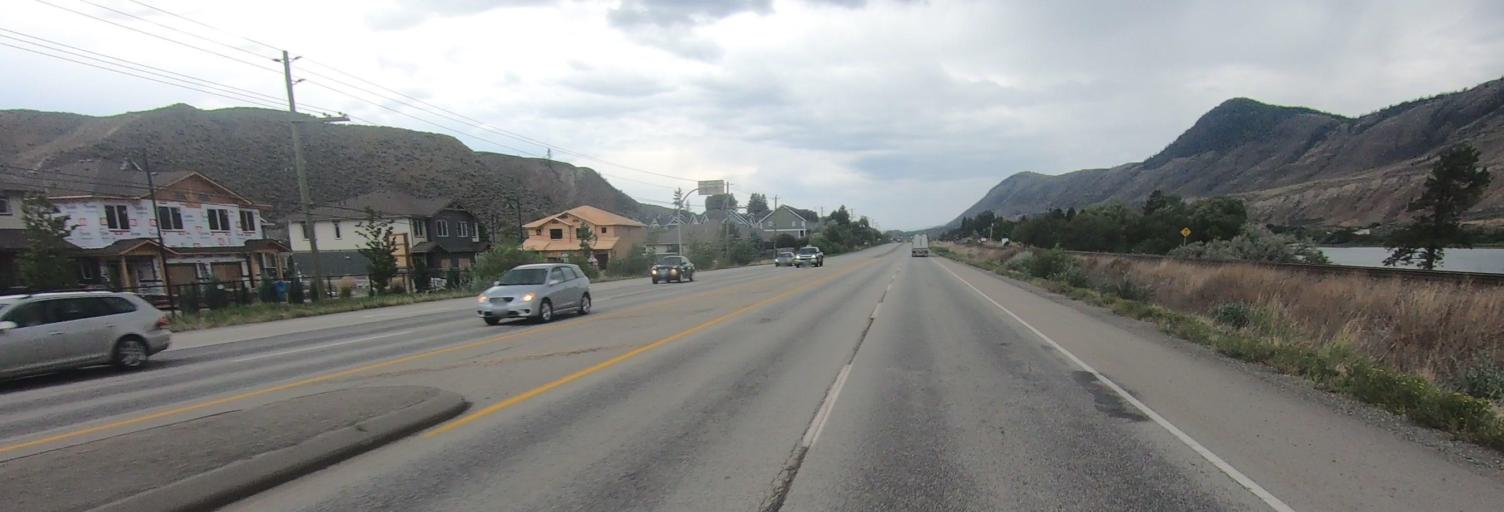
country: CA
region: British Columbia
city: Kamloops
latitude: 50.6722
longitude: -120.2271
